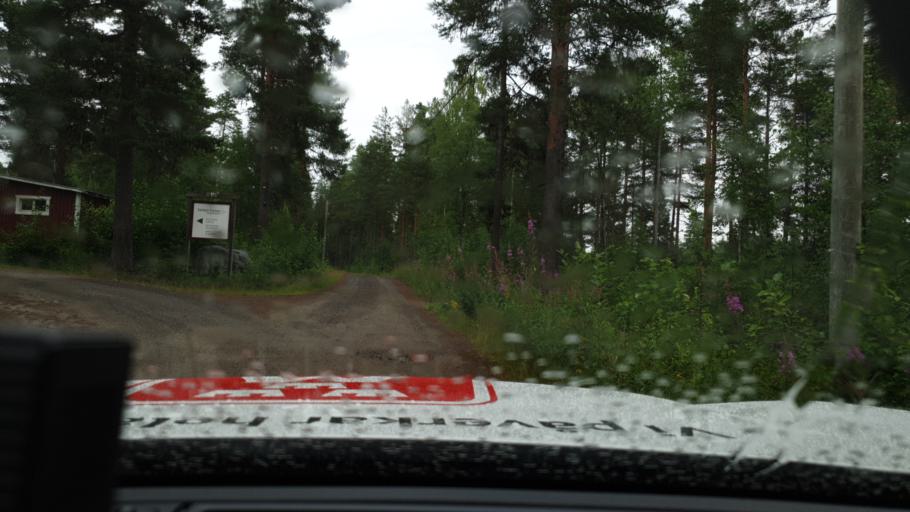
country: SE
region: Norrbotten
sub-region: Bodens Kommun
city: Boden
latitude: 66.0536
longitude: 21.7857
